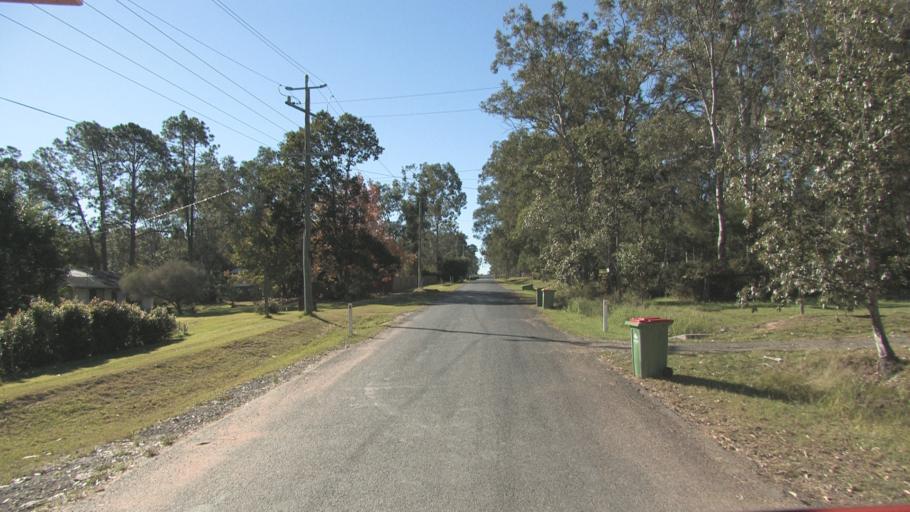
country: AU
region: Queensland
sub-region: Logan
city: Park Ridge South
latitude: -27.7319
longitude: 153.0112
